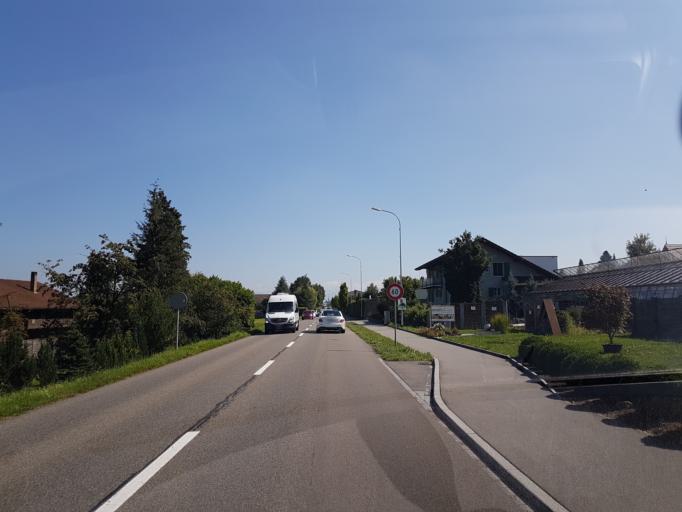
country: CH
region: Aargau
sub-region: Bezirk Muri
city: Buttwil
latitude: 47.2977
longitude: 8.3174
